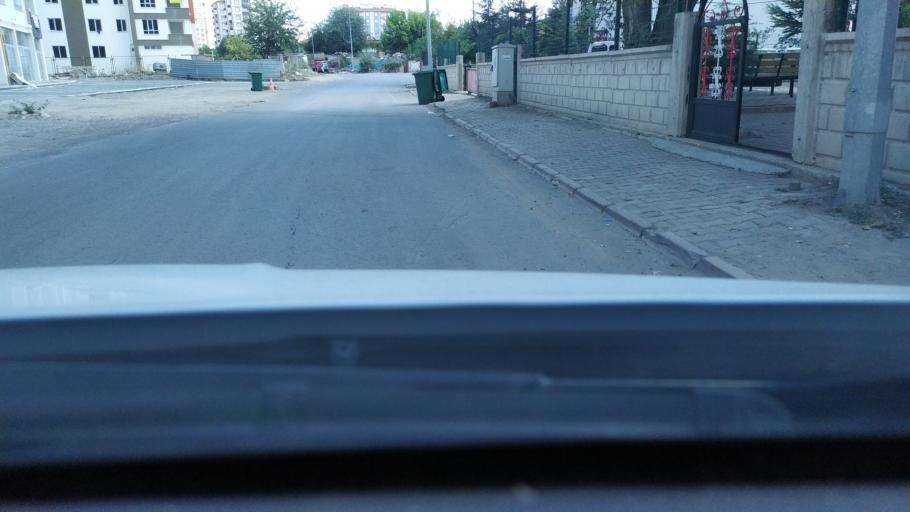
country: TR
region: Kayseri
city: Kayseri
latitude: 38.7101
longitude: 35.4734
